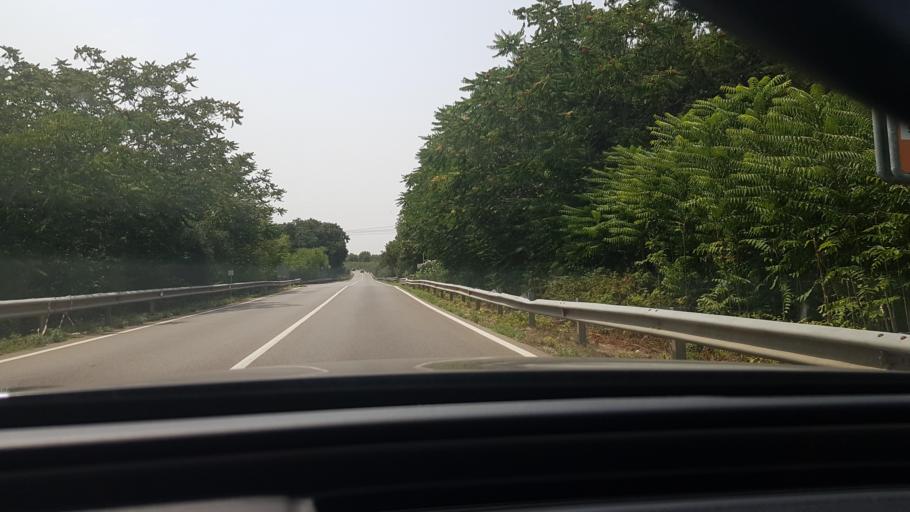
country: IT
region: Apulia
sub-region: Provincia di Barletta - Andria - Trani
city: Andria
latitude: 41.1525
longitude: 16.2927
